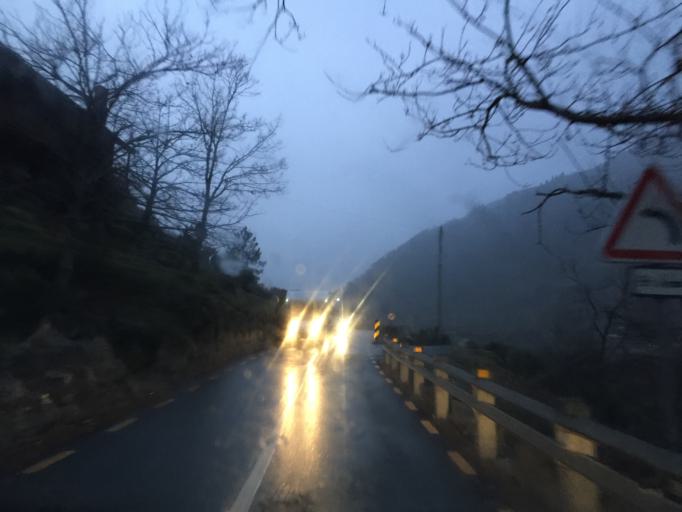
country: PT
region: Guarda
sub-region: Manteigas
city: Manteigas
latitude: 40.3797
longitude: -7.5459
